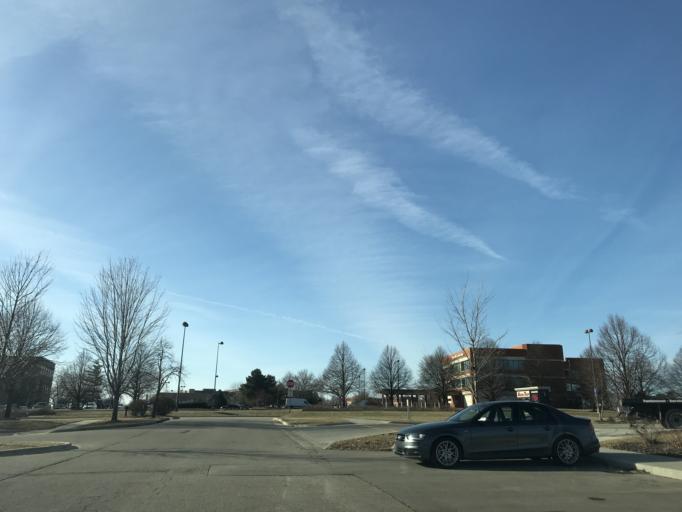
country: US
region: Wisconsin
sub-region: Dane County
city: Sun Prairie
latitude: 43.1490
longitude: -89.2892
